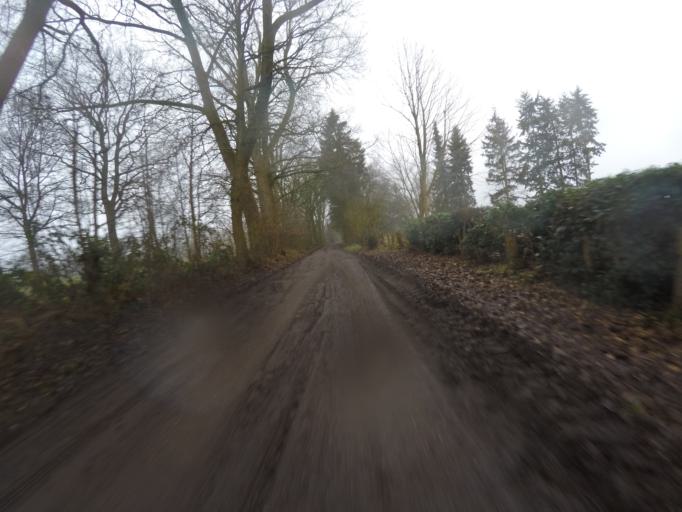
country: DE
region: Schleswig-Holstein
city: Ellerau
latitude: 53.7469
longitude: 9.9253
